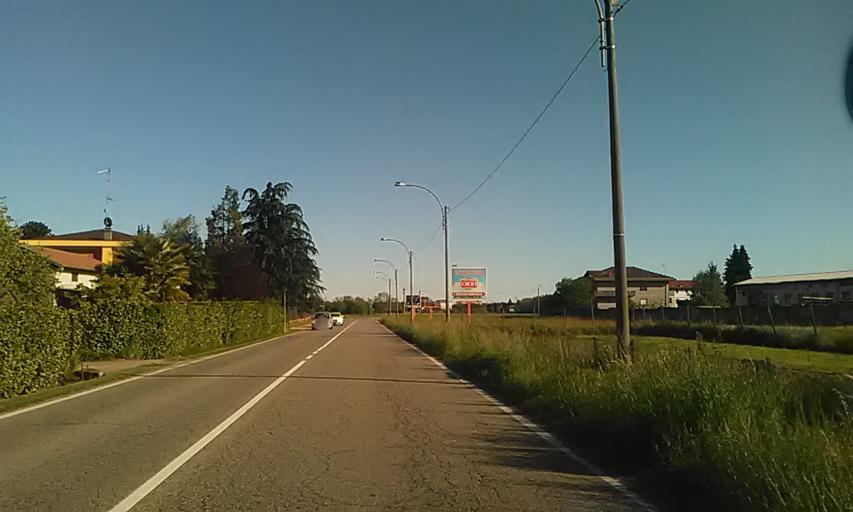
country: IT
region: Piedmont
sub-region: Provincia di Novara
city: Cavaglietto
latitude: 45.6150
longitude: 8.5186
